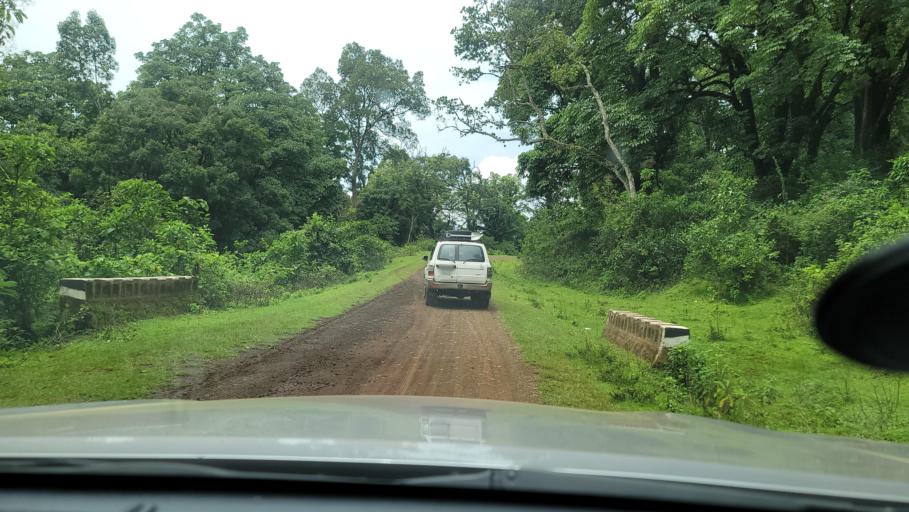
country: ET
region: Oromiya
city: Agaro
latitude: 7.7083
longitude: 36.2532
